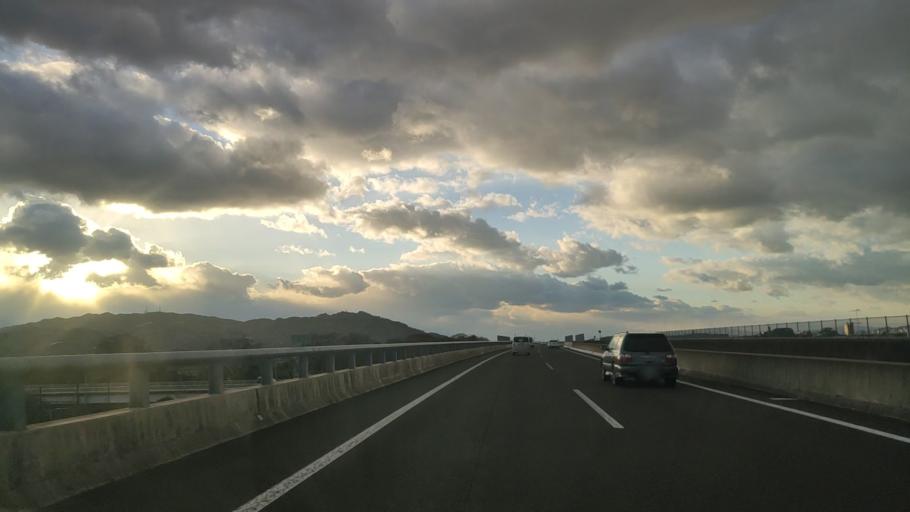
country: JP
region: Ehime
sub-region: Shikoku-chuo Shi
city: Matsuyama
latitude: 33.7875
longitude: 132.8156
